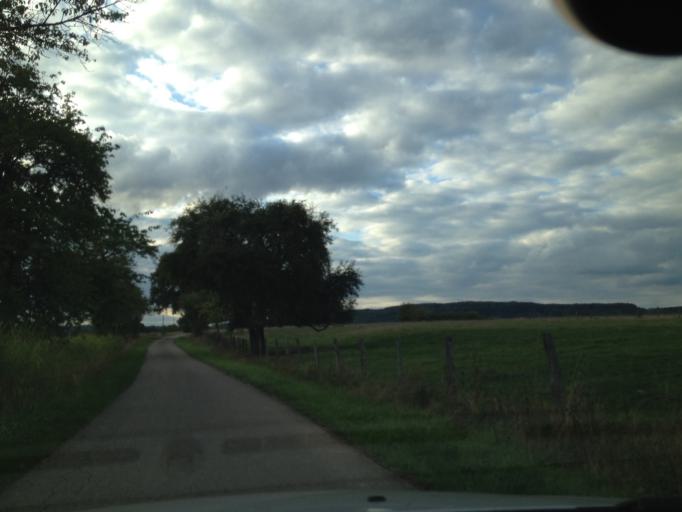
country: FR
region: Lorraine
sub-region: Departement des Vosges
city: Bains-les-Bains
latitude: 47.9829
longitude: 6.1974
